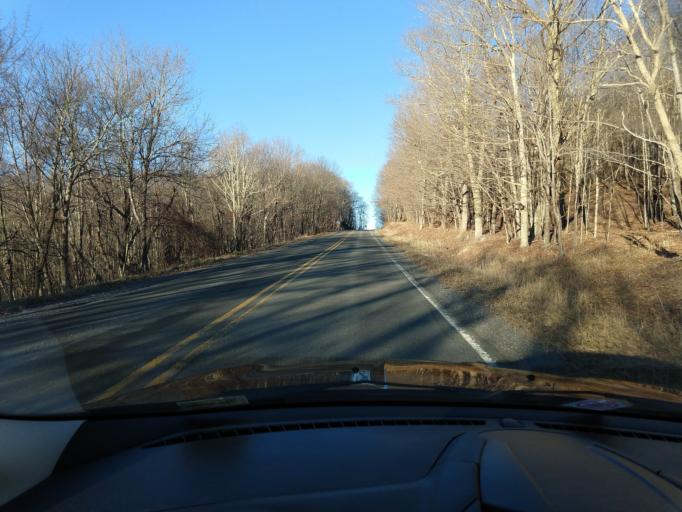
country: US
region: Virginia
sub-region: Highland County
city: Monterey
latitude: 38.4412
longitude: -79.6477
